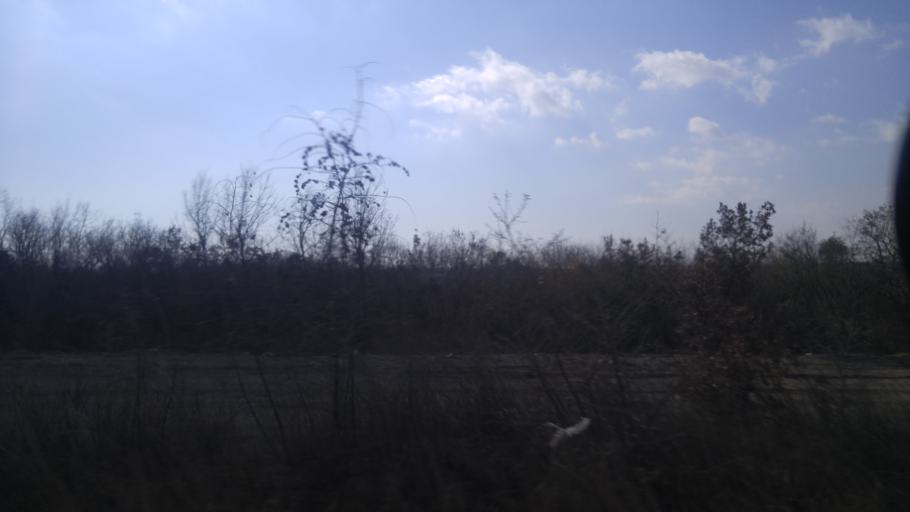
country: TR
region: Istanbul
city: Canta
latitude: 41.1663
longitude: 28.0999
